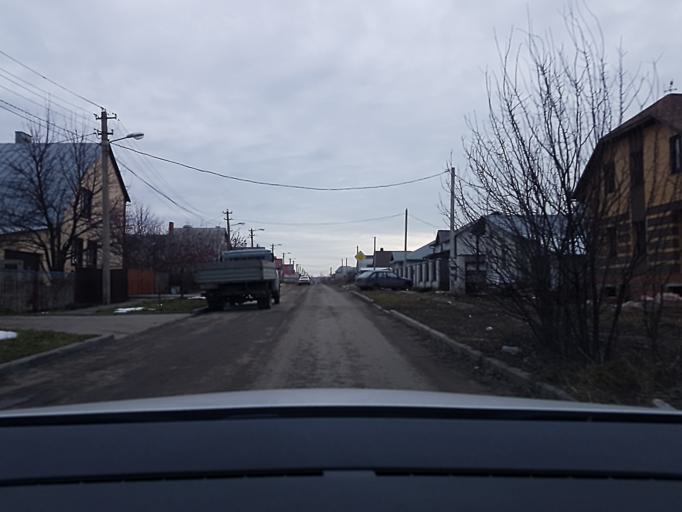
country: RU
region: Tambov
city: Tambov
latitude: 52.7834
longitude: 41.3756
